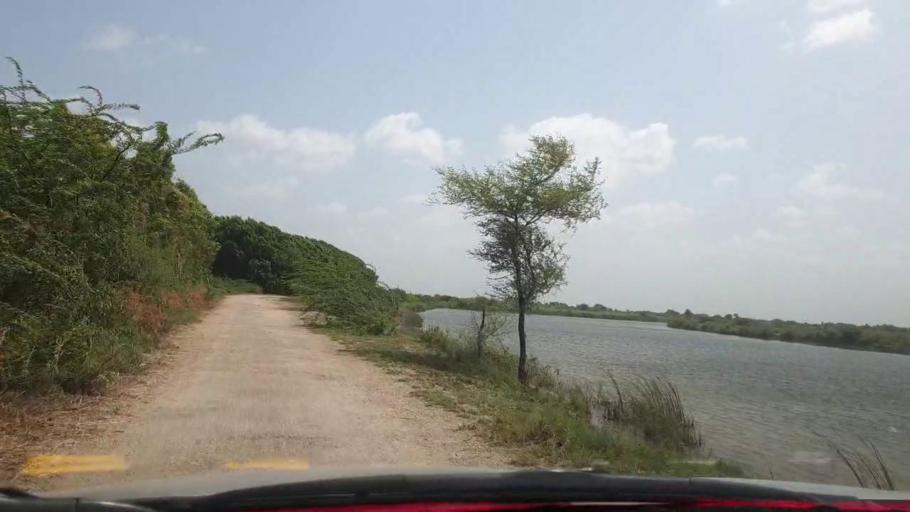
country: PK
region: Sindh
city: Tando Bago
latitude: 24.8686
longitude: 68.9179
